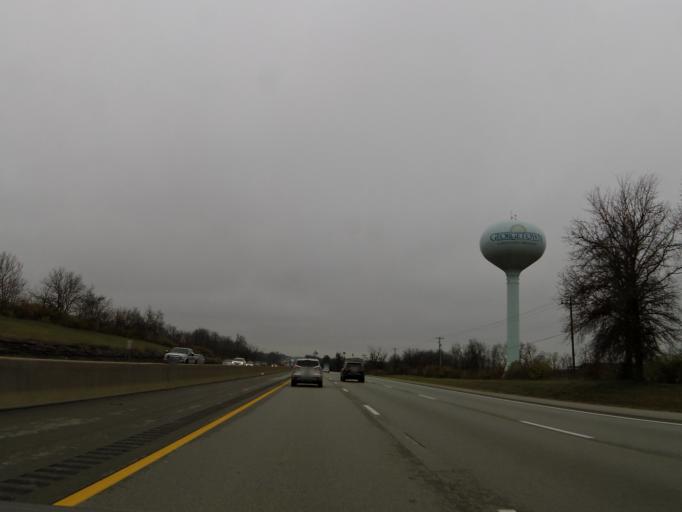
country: US
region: Kentucky
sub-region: Scott County
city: Georgetown
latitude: 38.2331
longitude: -84.5417
